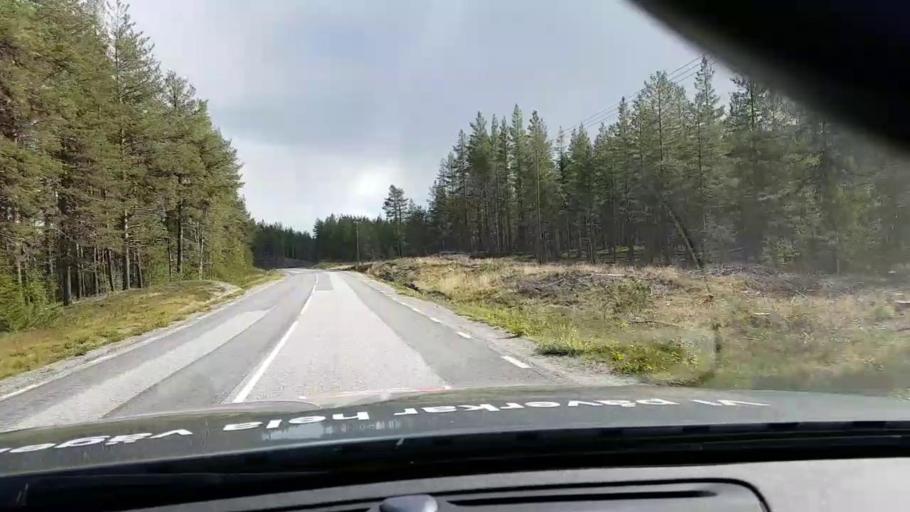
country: SE
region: Vaesterbotten
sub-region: Asele Kommun
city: Asele
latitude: 63.8551
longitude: 17.3885
